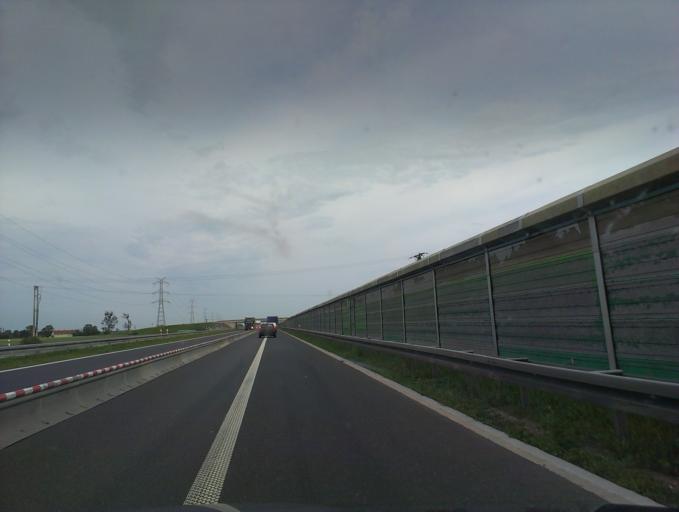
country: PL
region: Opole Voivodeship
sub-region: Powiat brzeski
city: Losiow
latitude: 50.7208
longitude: 17.5372
